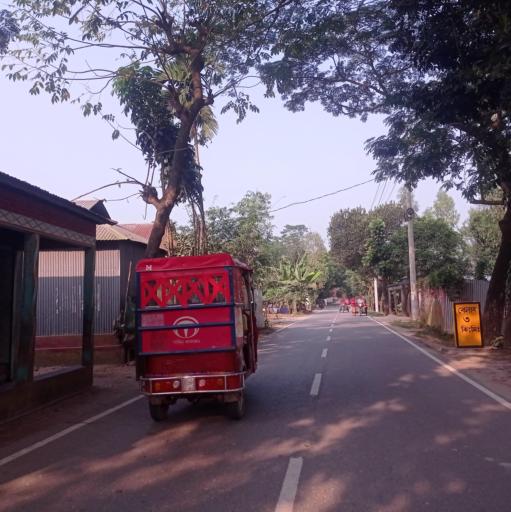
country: BD
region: Dhaka
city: Bhairab Bazar
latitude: 24.0920
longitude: 90.8502
